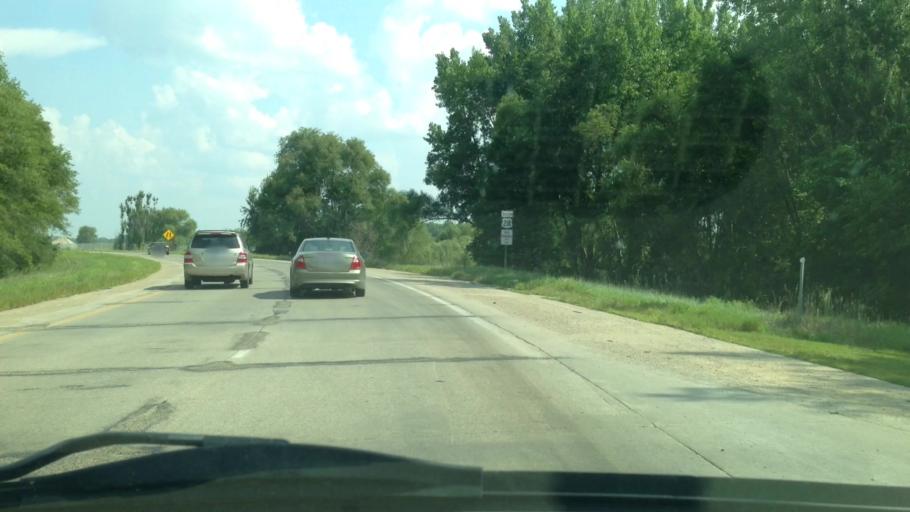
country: US
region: Iowa
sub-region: Black Hawk County
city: Cedar Falls
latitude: 42.5369
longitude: -92.3939
